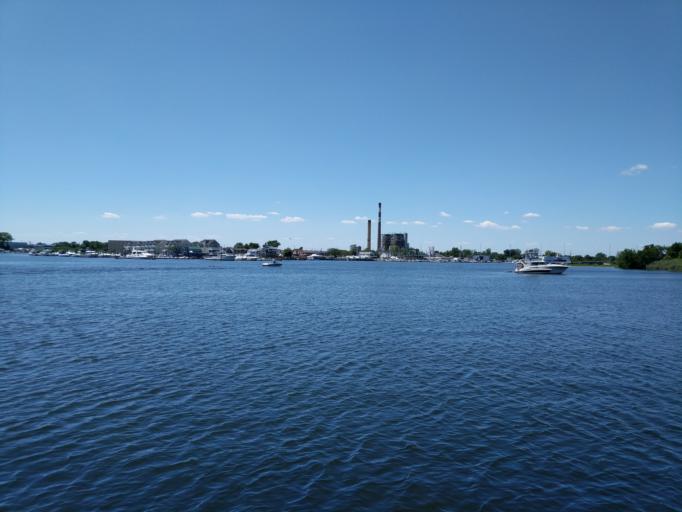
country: US
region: New York
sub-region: Nassau County
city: Barnum Island
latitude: 40.6125
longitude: -73.6371
